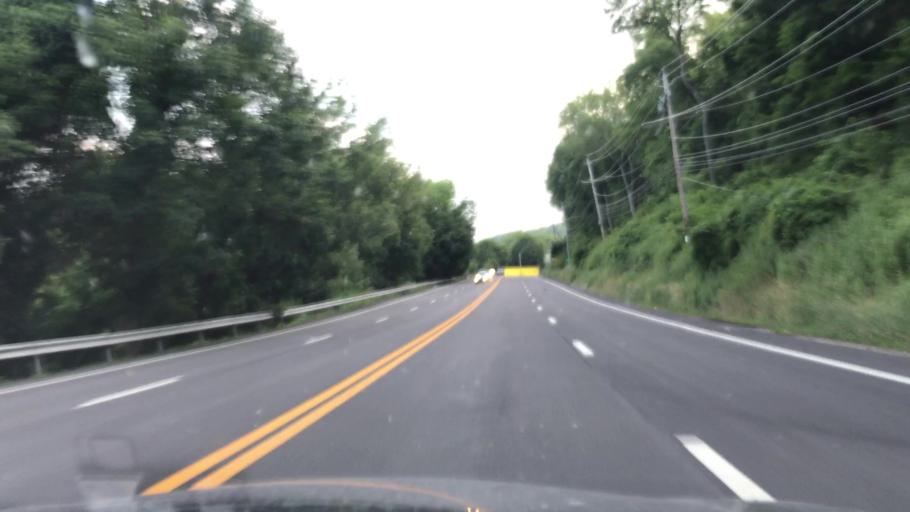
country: US
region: New York
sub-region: Orange County
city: Harriman
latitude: 41.2500
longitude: -74.1698
